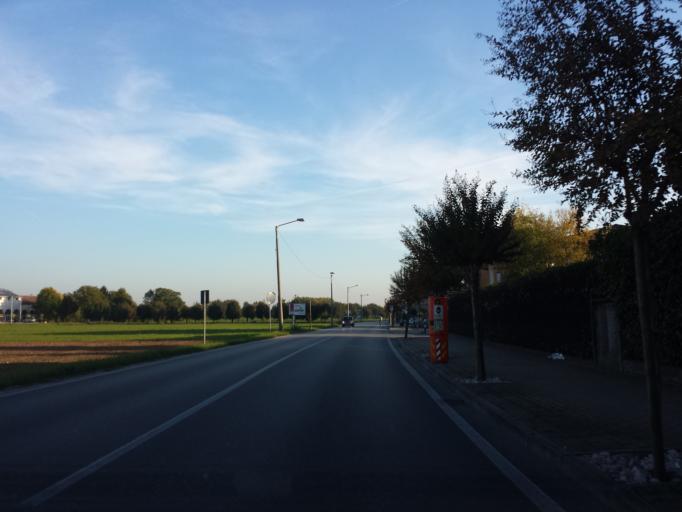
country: IT
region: Veneto
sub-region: Provincia di Vicenza
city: Crispi Cavour
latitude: 45.5872
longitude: 11.5318
